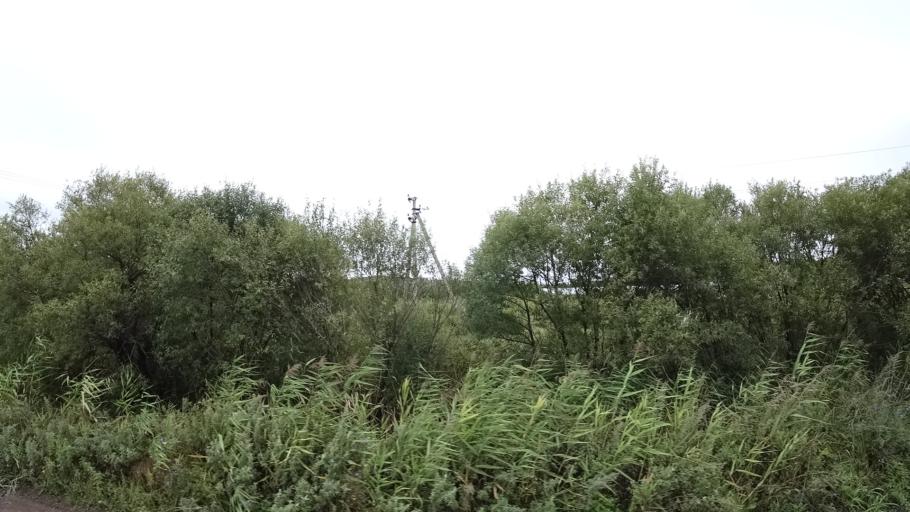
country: RU
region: Primorskiy
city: Monastyrishche
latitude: 44.1840
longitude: 132.4831
